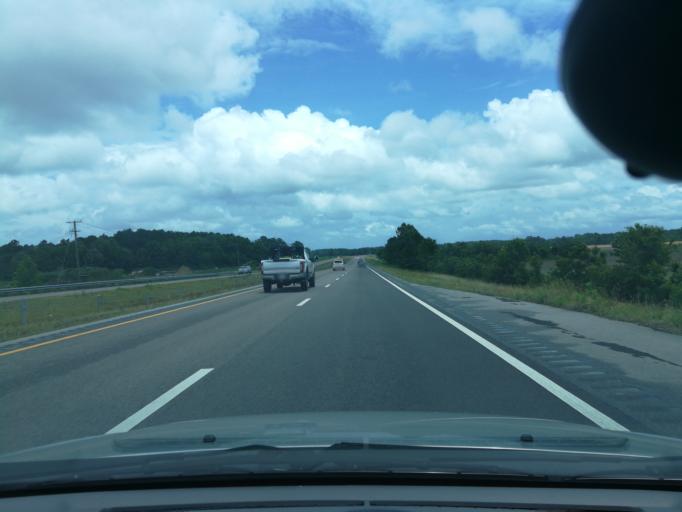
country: US
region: North Carolina
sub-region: Tyrrell County
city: Columbia
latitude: 35.8946
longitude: -76.3468
